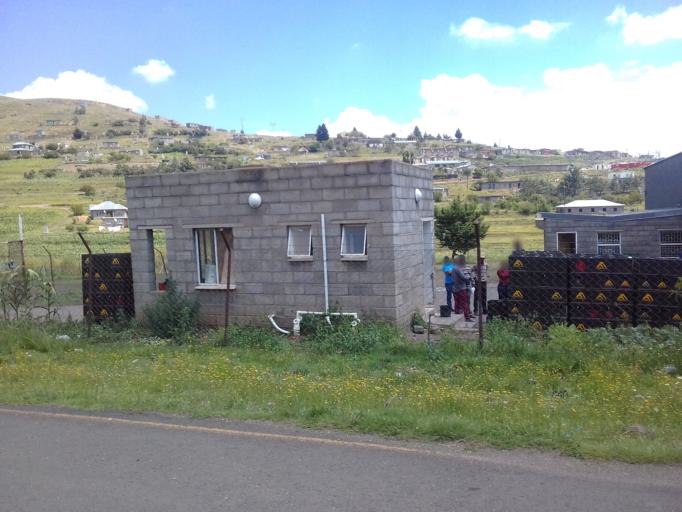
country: LS
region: Thaba-Tseka
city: Thaba-Tseka
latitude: -29.5198
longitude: 28.6068
